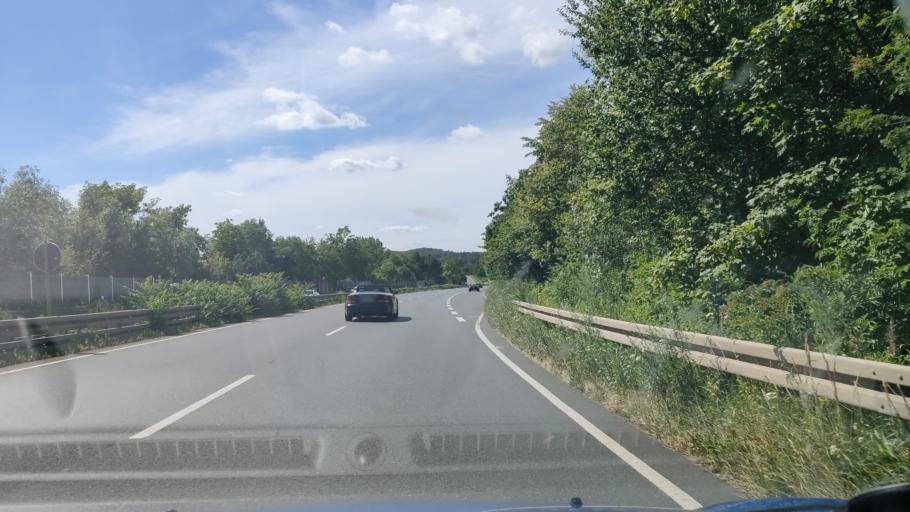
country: DE
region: Lower Saxony
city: Ronnenberg
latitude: 52.3479
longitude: 9.6625
